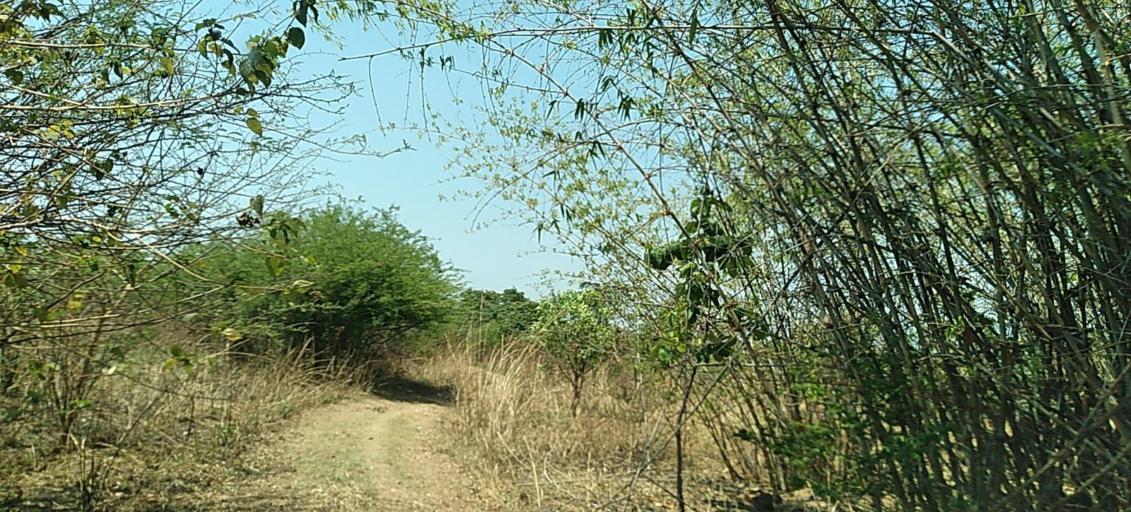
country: ZM
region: Copperbelt
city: Luanshya
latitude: -12.9880
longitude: 28.3261
